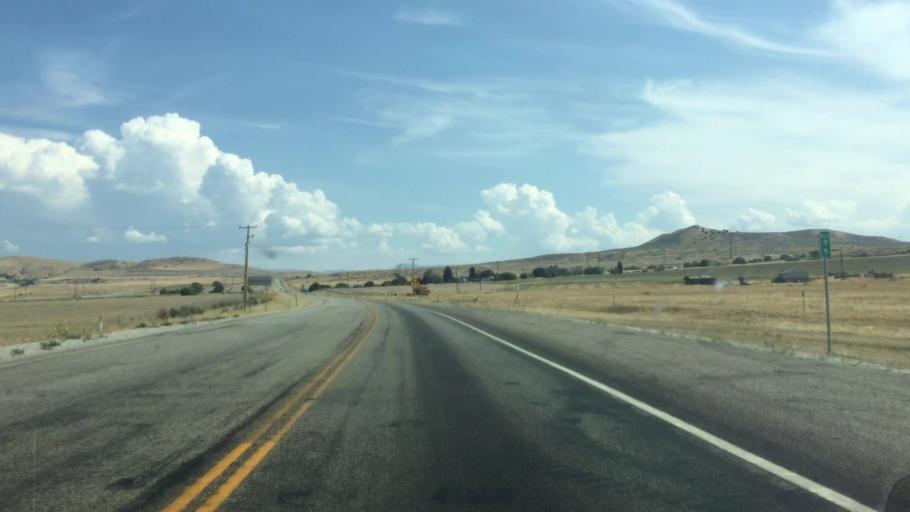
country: US
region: Utah
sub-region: Box Elder County
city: Garland
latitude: 41.7863
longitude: -112.0880
